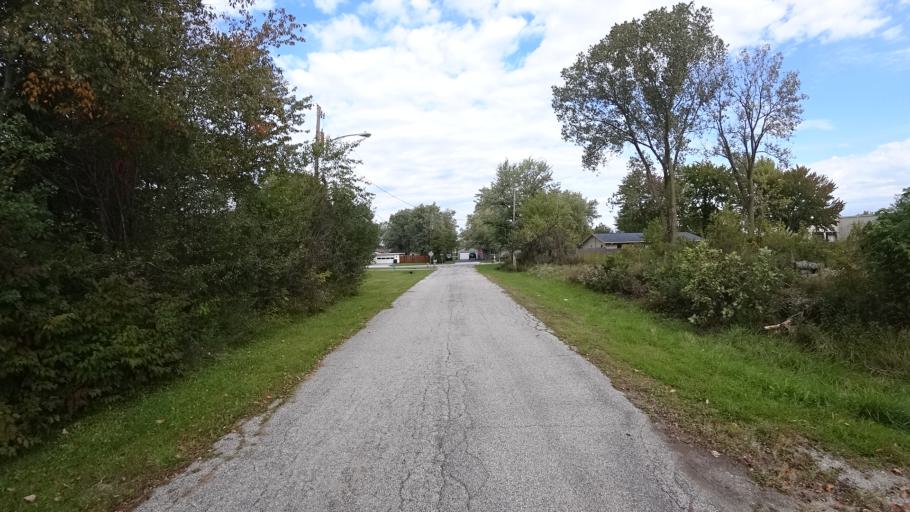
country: US
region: Indiana
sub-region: LaPorte County
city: Michigan City
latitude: 41.6710
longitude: -86.8966
